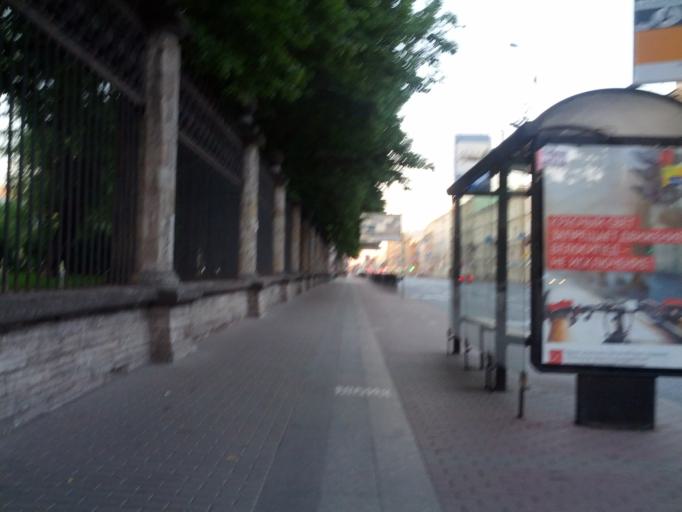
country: RU
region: St.-Petersburg
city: Saint Petersburg
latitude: 59.9133
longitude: 30.3184
